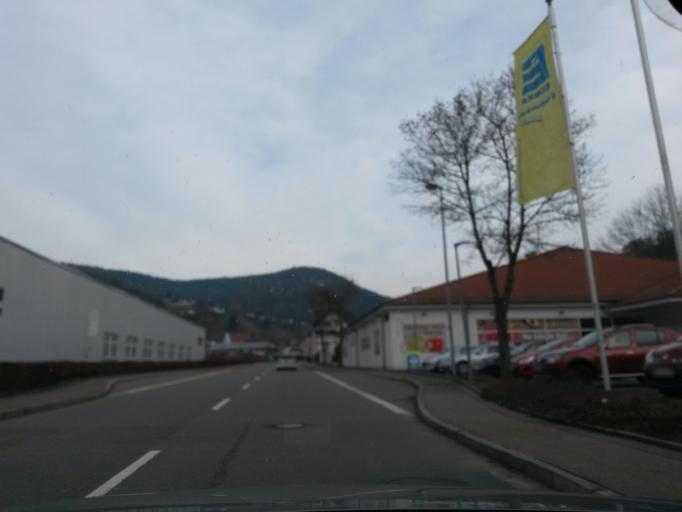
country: DE
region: Baden-Wuerttemberg
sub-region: Karlsruhe Region
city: Alpirsbach
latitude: 48.3402
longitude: 8.3965
